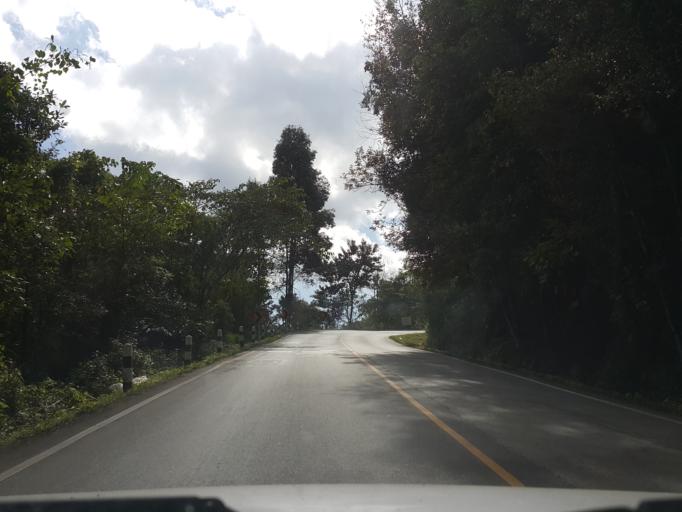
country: TH
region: Mae Hong Son
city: Mae Hi
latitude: 19.2755
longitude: 98.6096
